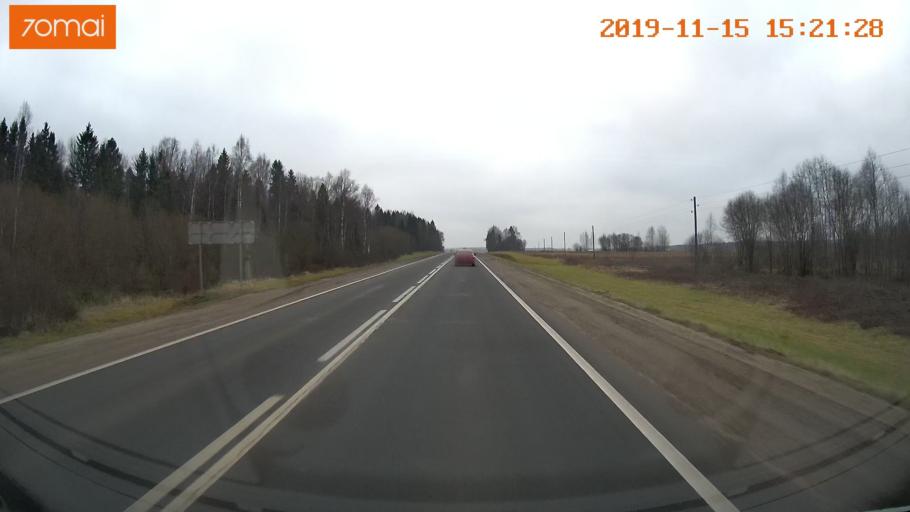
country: RU
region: Jaroslavl
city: Danilov
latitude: 58.2122
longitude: 40.1450
